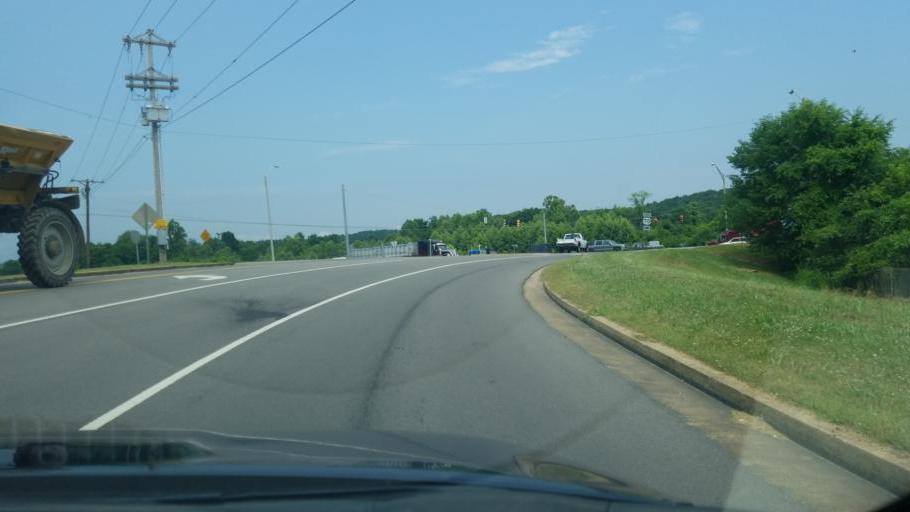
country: US
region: Tennessee
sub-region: Humphreys County
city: Waverly
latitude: 36.0790
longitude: -87.8356
